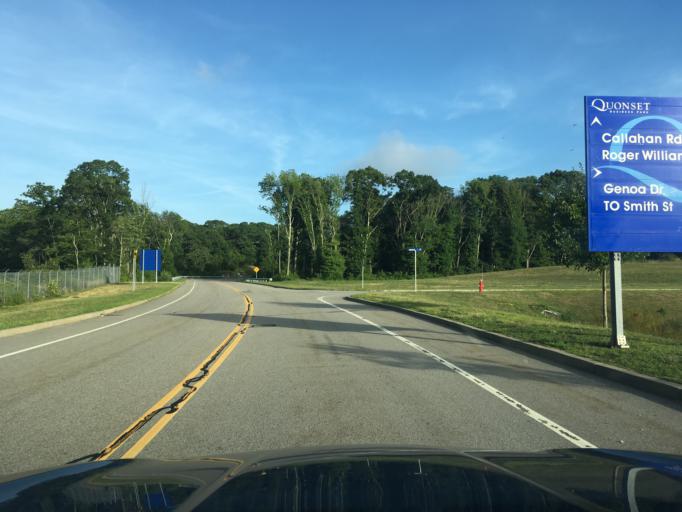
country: US
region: Rhode Island
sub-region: Kent County
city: East Greenwich
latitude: 41.6054
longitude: -71.4276
